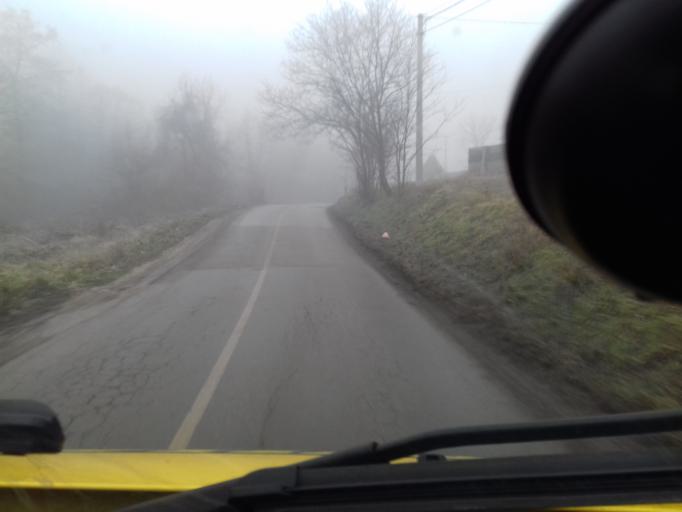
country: BA
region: Federation of Bosnia and Herzegovina
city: Lokvine
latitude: 44.2190
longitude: 17.8631
